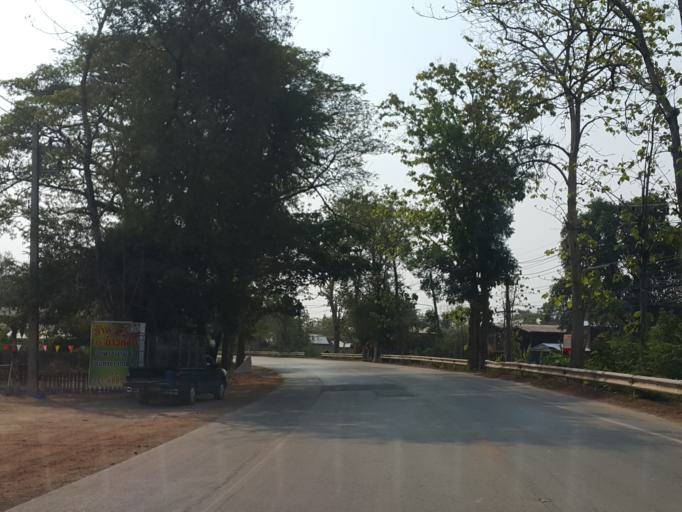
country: TH
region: Sukhothai
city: Ban Na
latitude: 17.0220
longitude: 99.6876
